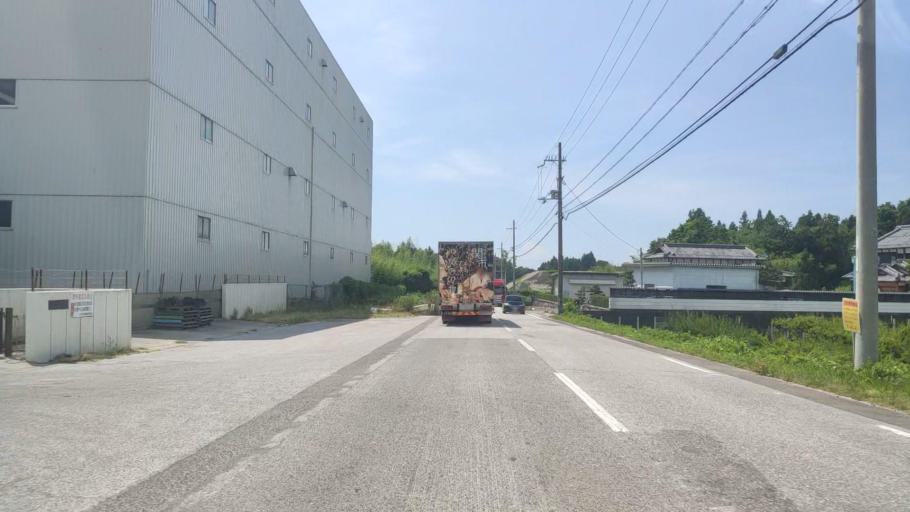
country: JP
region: Shiga Prefecture
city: Nagahama
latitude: 35.3703
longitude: 136.3970
